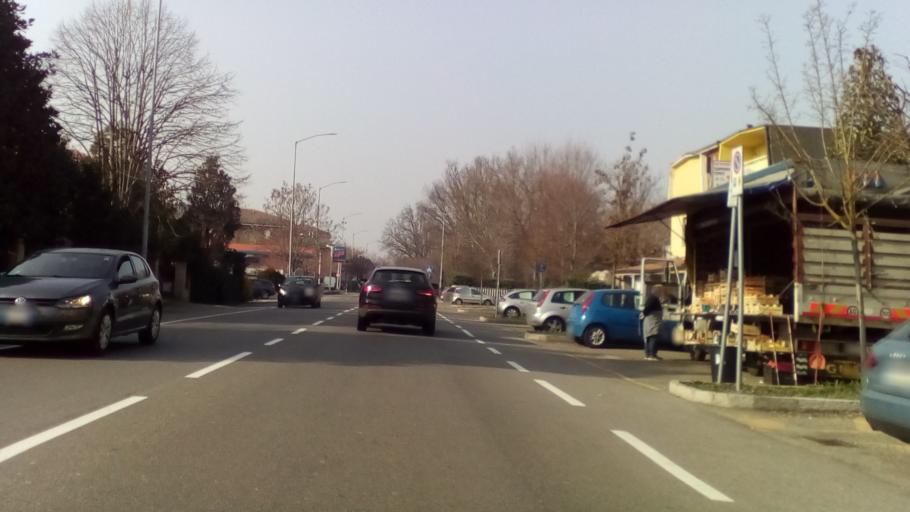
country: IT
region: Emilia-Romagna
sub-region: Provincia di Modena
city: Modena
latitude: 44.6265
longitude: 10.9486
